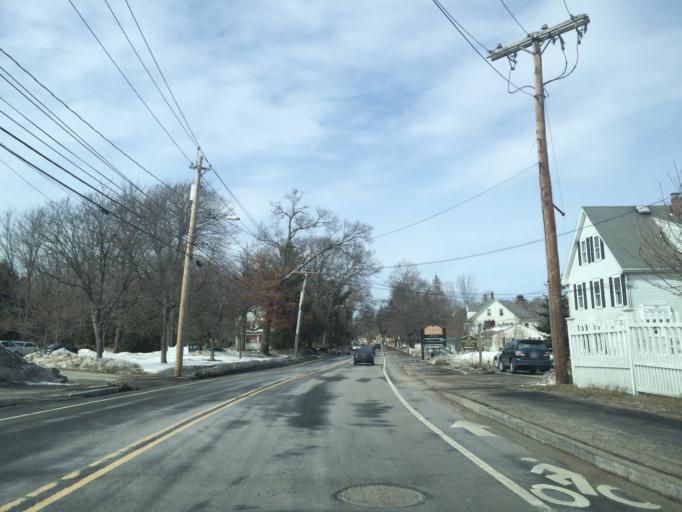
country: US
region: Massachusetts
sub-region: Middlesex County
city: Lexington
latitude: 42.4589
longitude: -71.2379
